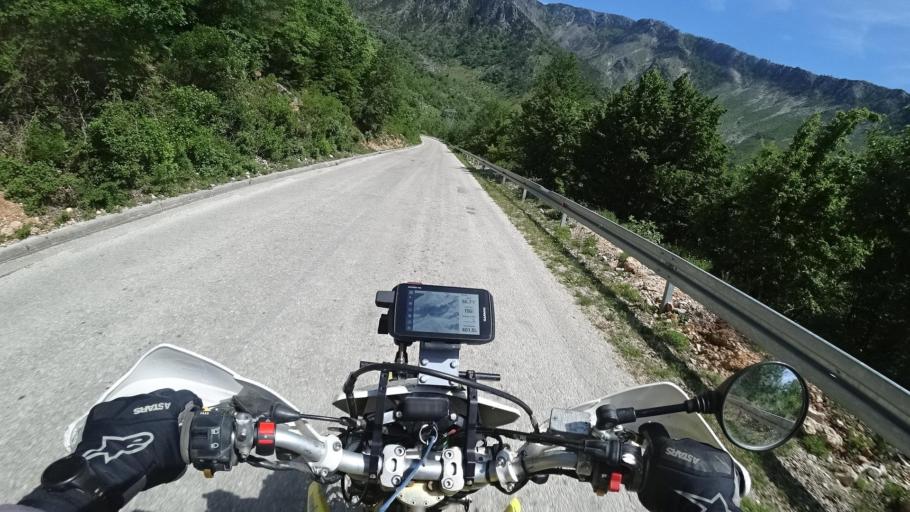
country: BA
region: Federation of Bosnia and Herzegovina
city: Potoci
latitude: 43.4545
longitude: 17.9435
